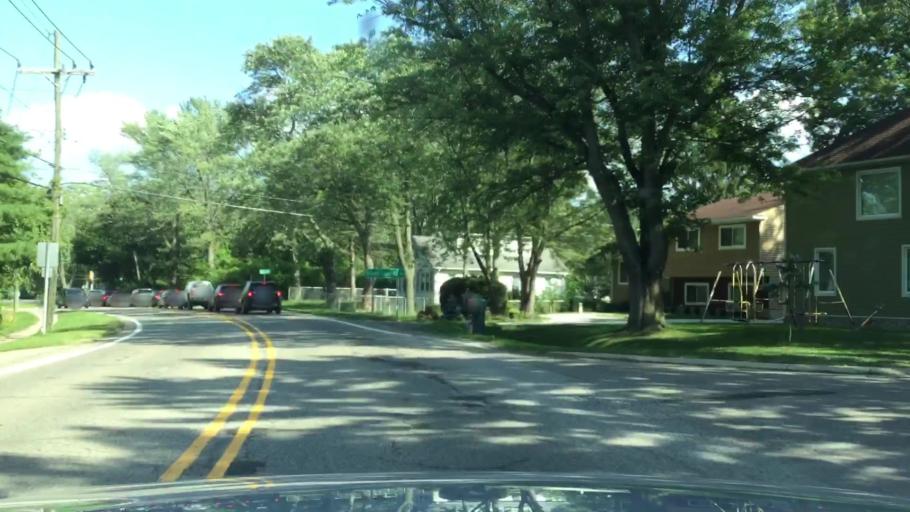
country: US
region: Michigan
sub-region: Oakland County
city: West Bloomfield Township
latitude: 42.5747
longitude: -83.4232
